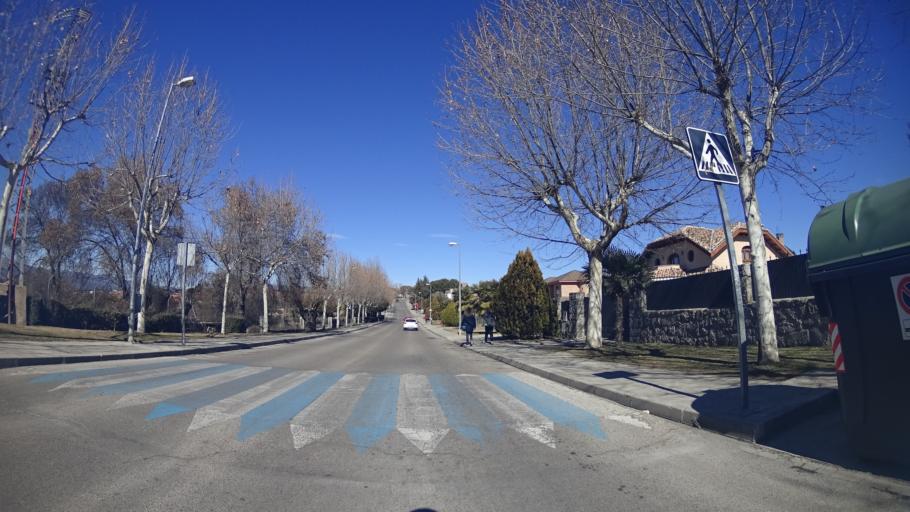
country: ES
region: Madrid
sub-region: Provincia de Madrid
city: Colmenarejo
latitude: 40.5541
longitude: -4.0132
